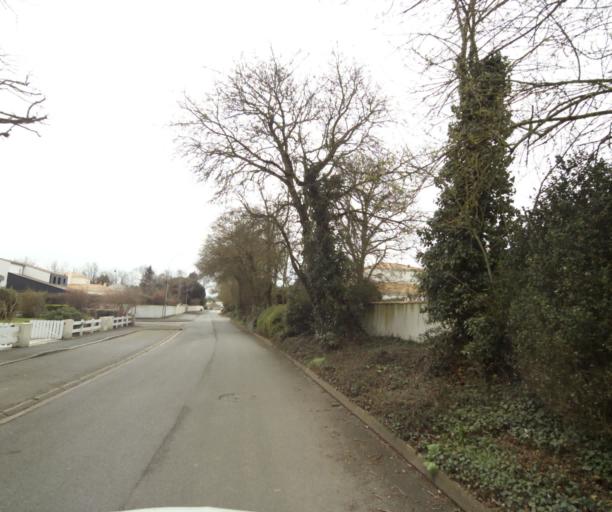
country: FR
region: Poitou-Charentes
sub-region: Departement de la Charente-Maritime
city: Lagord
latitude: 46.1876
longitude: -1.1665
